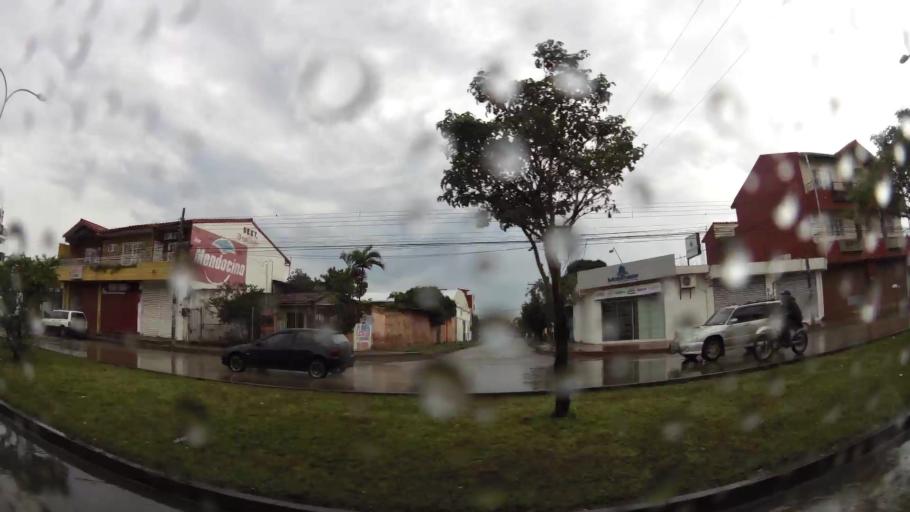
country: BO
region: Santa Cruz
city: Santa Cruz de la Sierra
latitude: -17.7672
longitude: -63.1517
